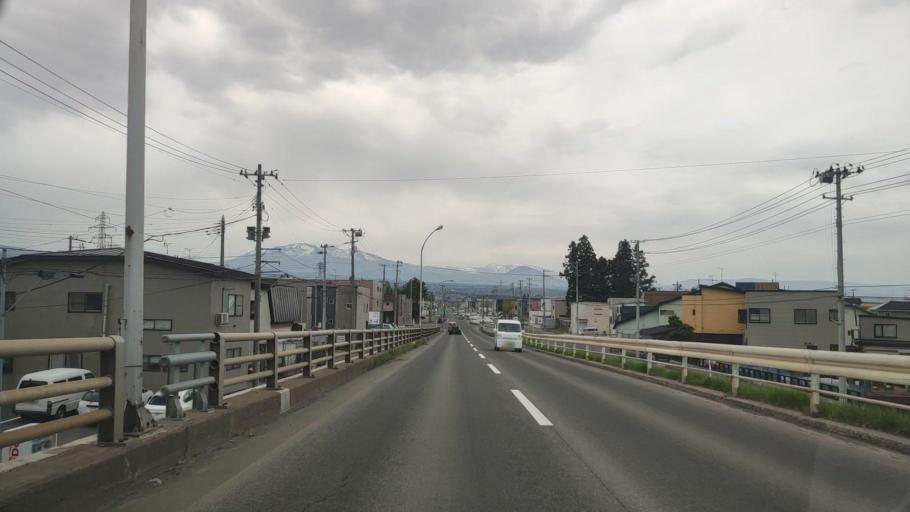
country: JP
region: Aomori
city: Aomori Shi
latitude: 40.8072
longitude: 140.7801
